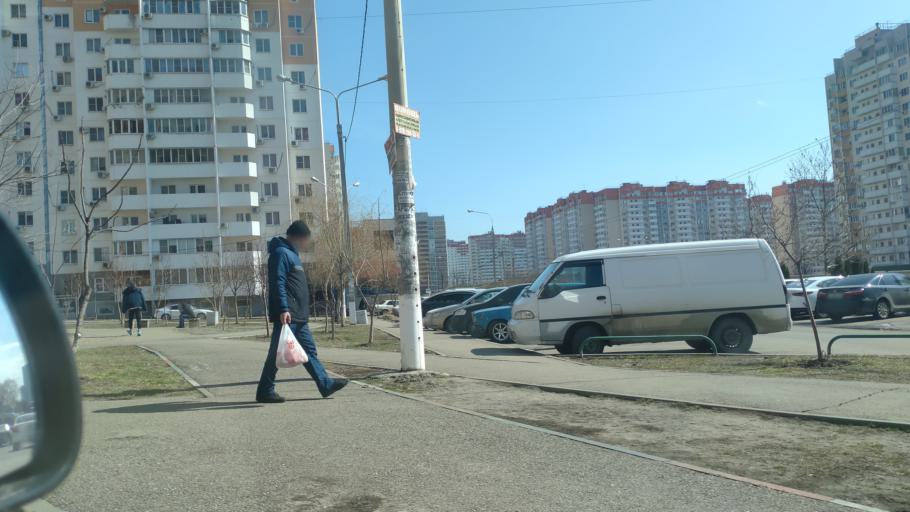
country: RU
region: Krasnodarskiy
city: Krasnodar
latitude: 45.0597
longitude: 39.0282
